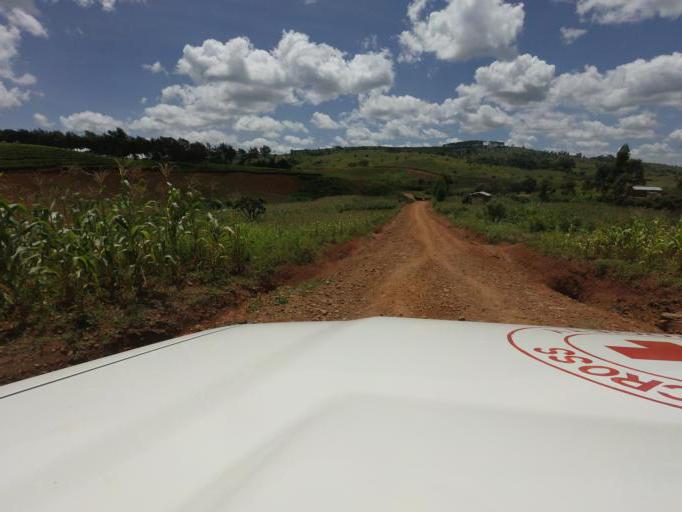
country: MW
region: Southern Region
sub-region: Thyolo District
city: Thyolo
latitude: -16.0316
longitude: 35.0553
